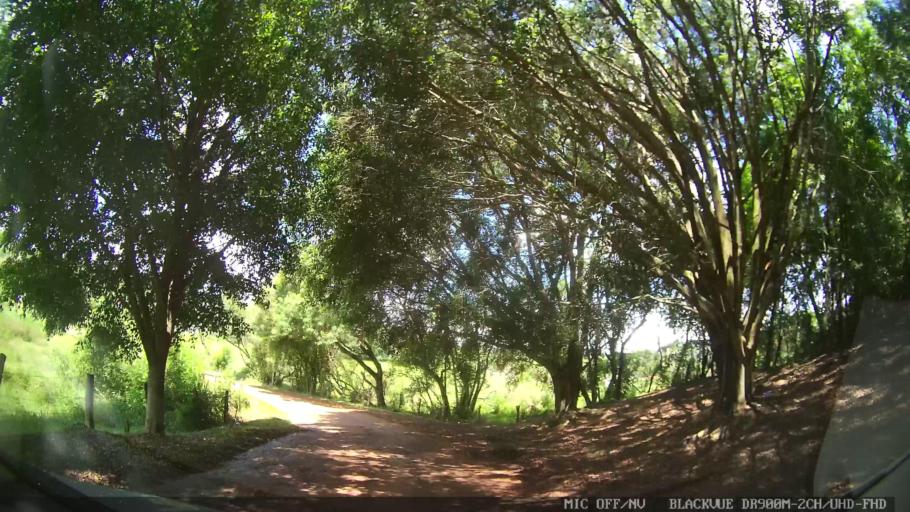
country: BR
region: Sao Paulo
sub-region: Amparo
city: Amparo
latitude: -22.8049
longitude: -46.7014
